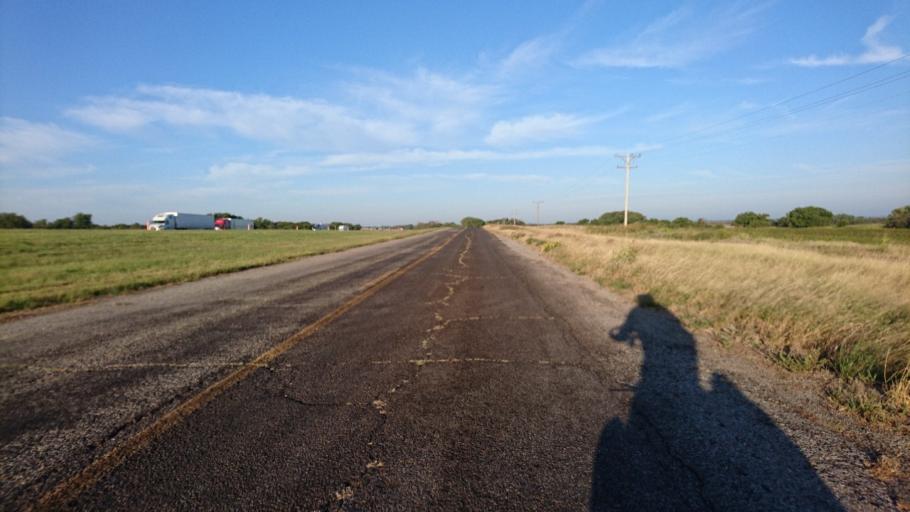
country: US
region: Oklahoma
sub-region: Beckham County
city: Sayre
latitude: 35.2625
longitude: -99.7019
